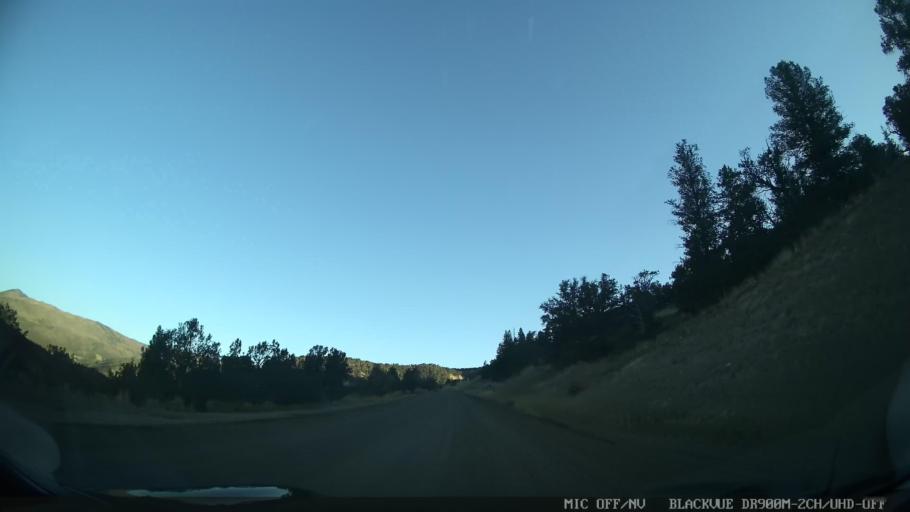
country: US
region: Colorado
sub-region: Grand County
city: Kremmling
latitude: 39.9424
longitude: -106.5283
